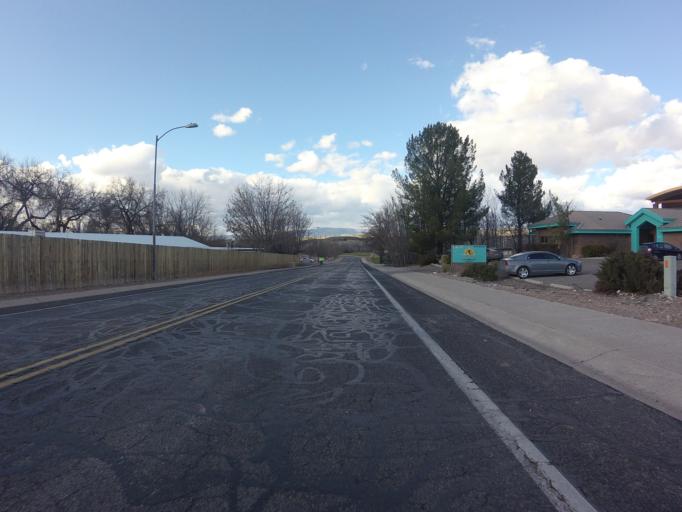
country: US
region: Arizona
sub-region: Yavapai County
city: Cottonwood
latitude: 34.7447
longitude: -112.0165
